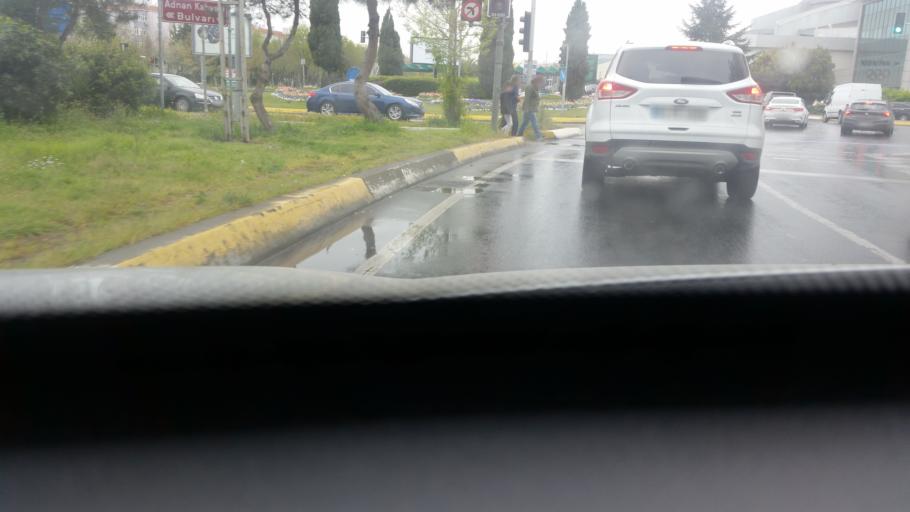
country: TR
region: Istanbul
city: Bahcelievler
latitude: 40.9860
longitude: 28.8530
